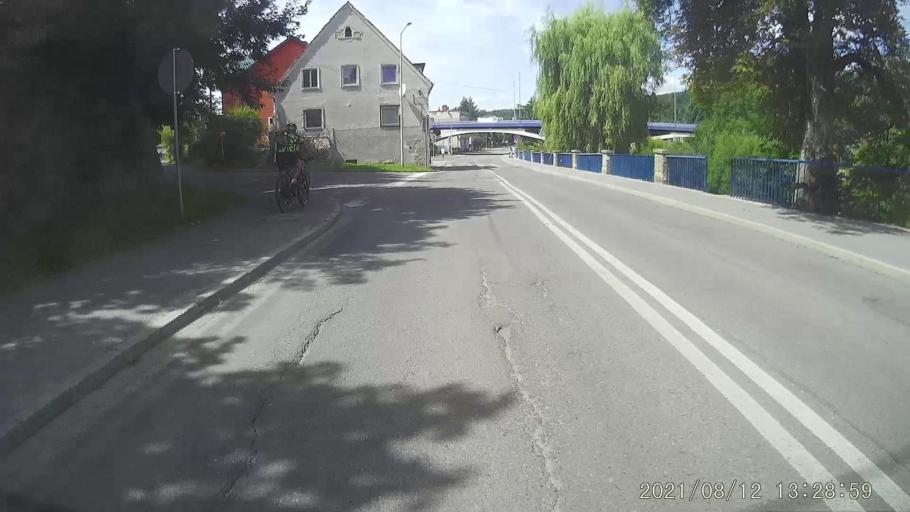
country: PL
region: Lower Silesian Voivodeship
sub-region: Powiat klodzki
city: Ladek-Zdroj
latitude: 50.3430
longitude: 16.8808
